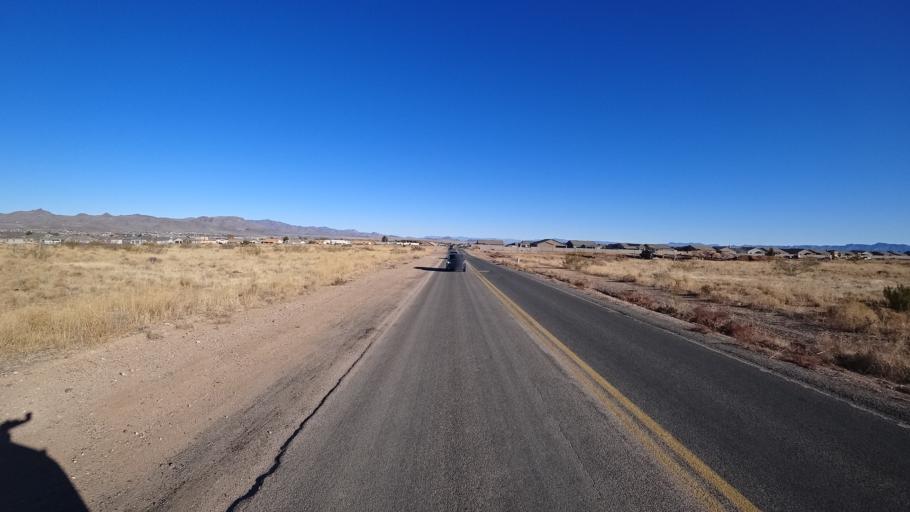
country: US
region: Arizona
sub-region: Mohave County
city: Kingman
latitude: 35.1889
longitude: -114.0026
